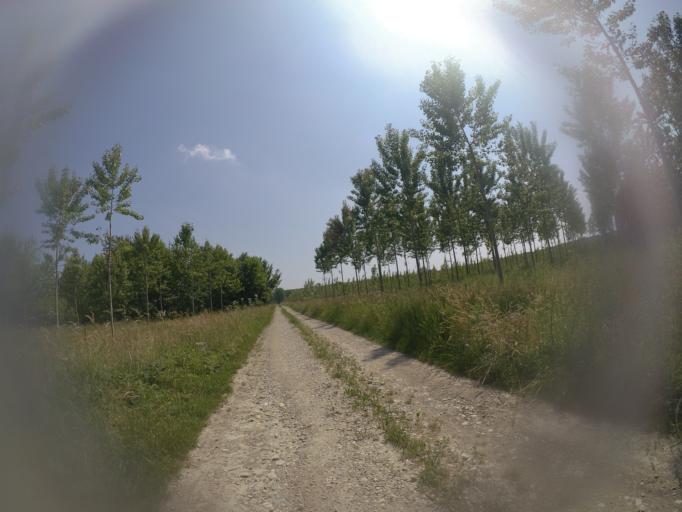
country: IT
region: Friuli Venezia Giulia
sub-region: Provincia di Udine
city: Bertiolo
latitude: 45.9294
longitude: 13.0263
